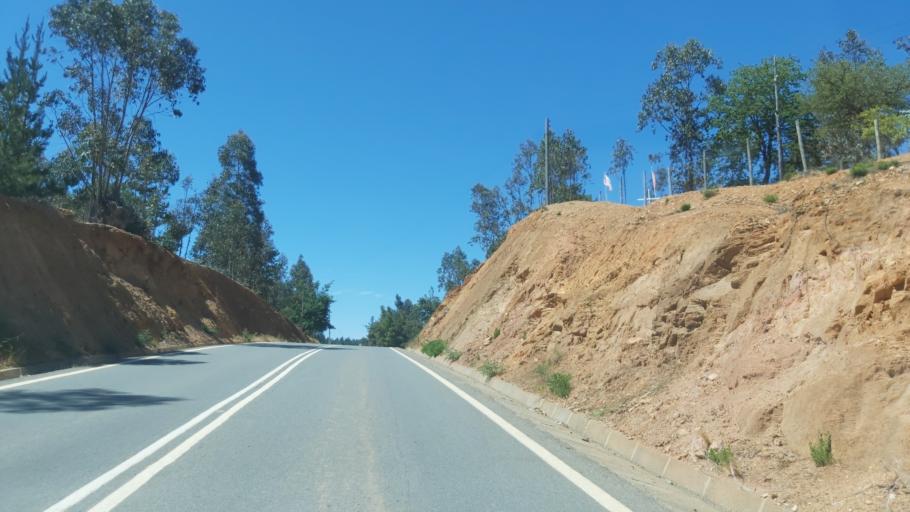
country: CL
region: Maule
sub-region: Provincia de Talca
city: Constitucion
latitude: -34.9175
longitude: -71.9925
